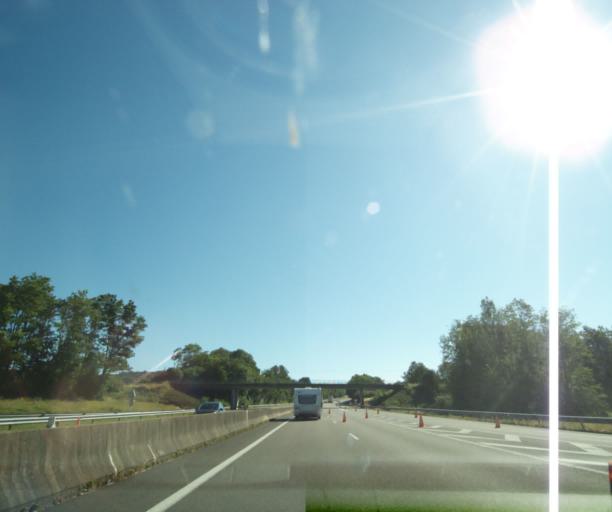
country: FR
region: Champagne-Ardenne
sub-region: Departement de la Haute-Marne
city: Rolampont
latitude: 47.9444
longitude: 5.3038
